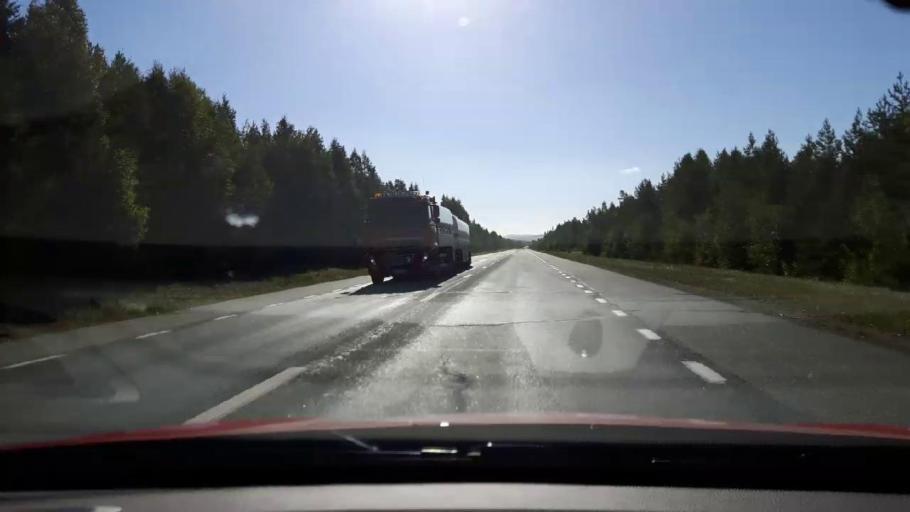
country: SE
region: Vaesternorrland
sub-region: Ange Kommun
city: Ange
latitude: 62.5927
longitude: 15.7108
